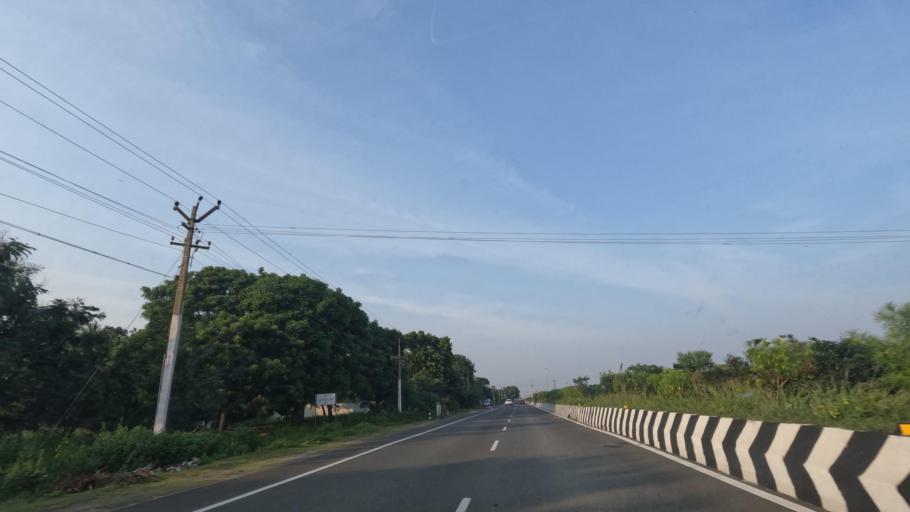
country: IN
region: Tamil Nadu
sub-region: Kancheepuram
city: Mamallapuram
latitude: 12.6851
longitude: 80.2155
